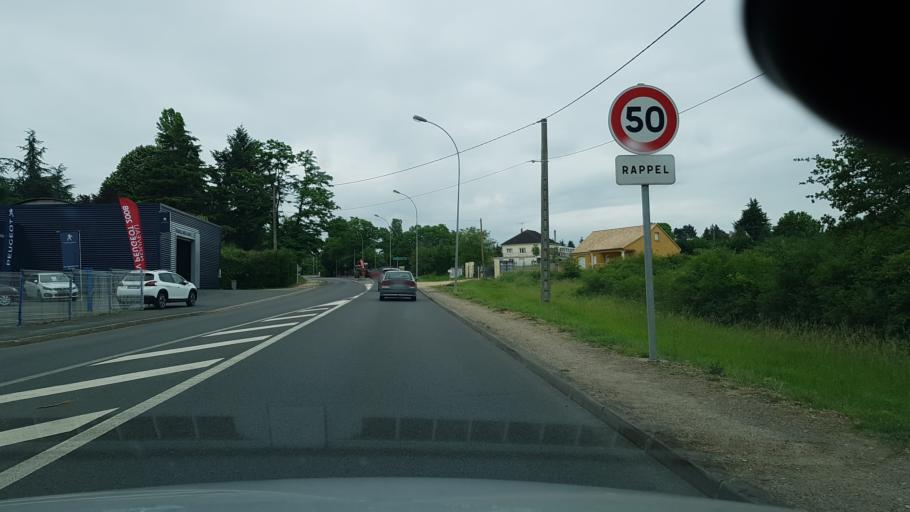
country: FR
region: Centre
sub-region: Departement du Loir-et-Cher
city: Selles-sur-Cher
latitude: 47.2846
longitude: 1.5394
